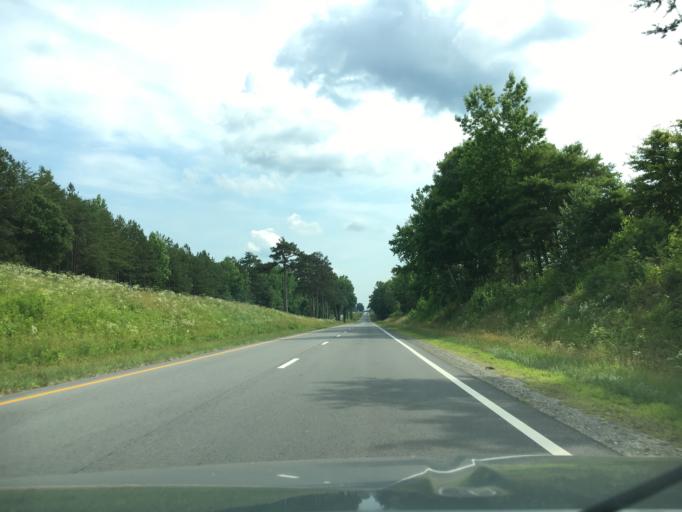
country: US
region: Virginia
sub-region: Mecklenburg County
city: Chase City
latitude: 36.9520
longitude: -78.4992
